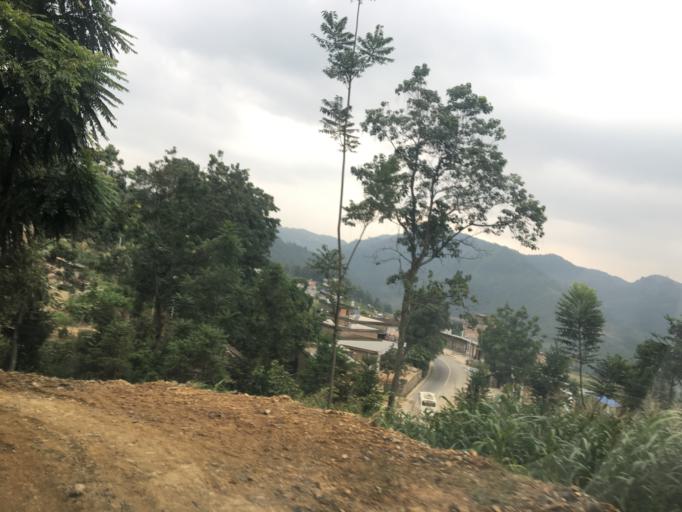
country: CN
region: Guangxi Zhuangzu Zizhiqu
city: Xinzhou
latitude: 25.1684
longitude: 105.6852
